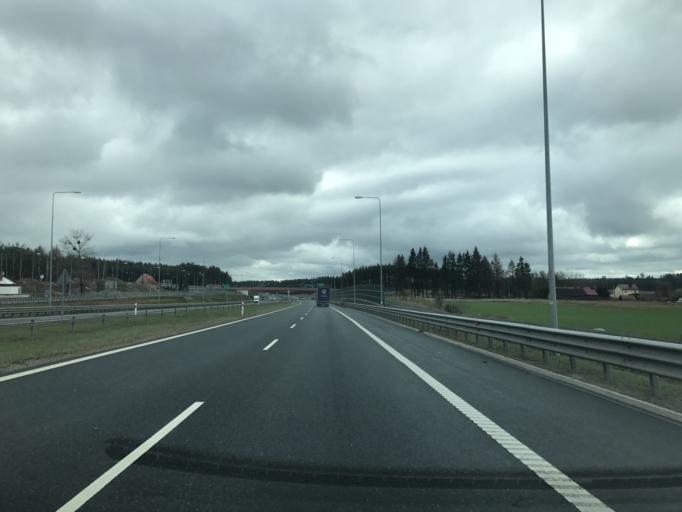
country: PL
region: Warmian-Masurian Voivodeship
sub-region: Powiat olsztynski
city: Olsztynek
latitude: 53.5365
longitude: 20.2739
